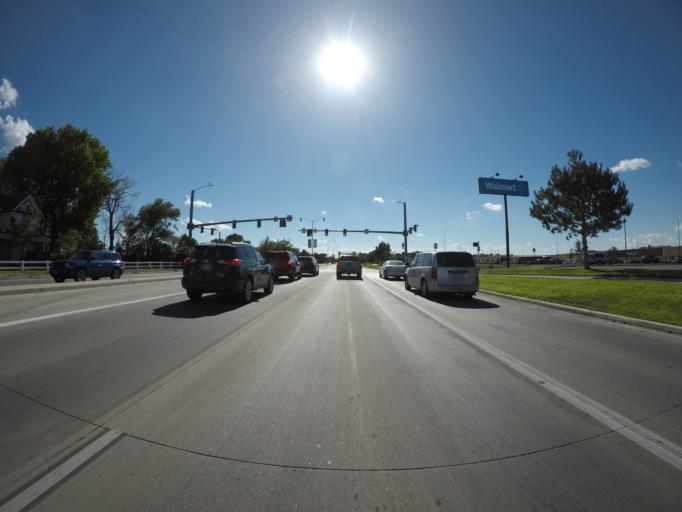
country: US
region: Colorado
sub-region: Logan County
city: Sterling
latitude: 40.6251
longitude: -103.2347
